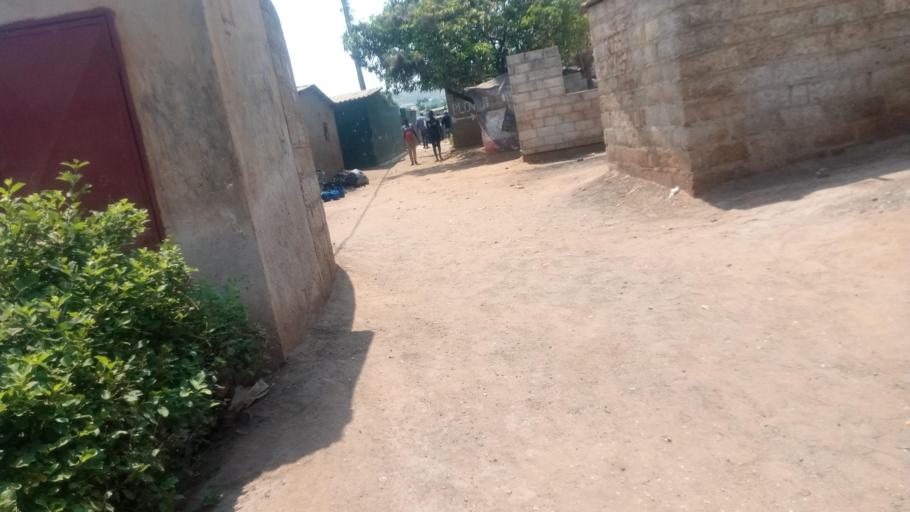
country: ZM
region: Lusaka
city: Lusaka
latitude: -15.4464
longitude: 28.3816
